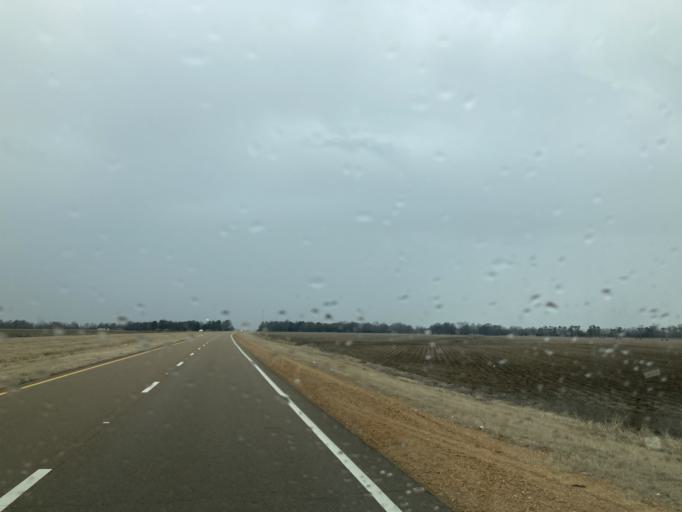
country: US
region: Mississippi
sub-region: Humphreys County
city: Belzoni
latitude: 33.0833
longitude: -90.4844
